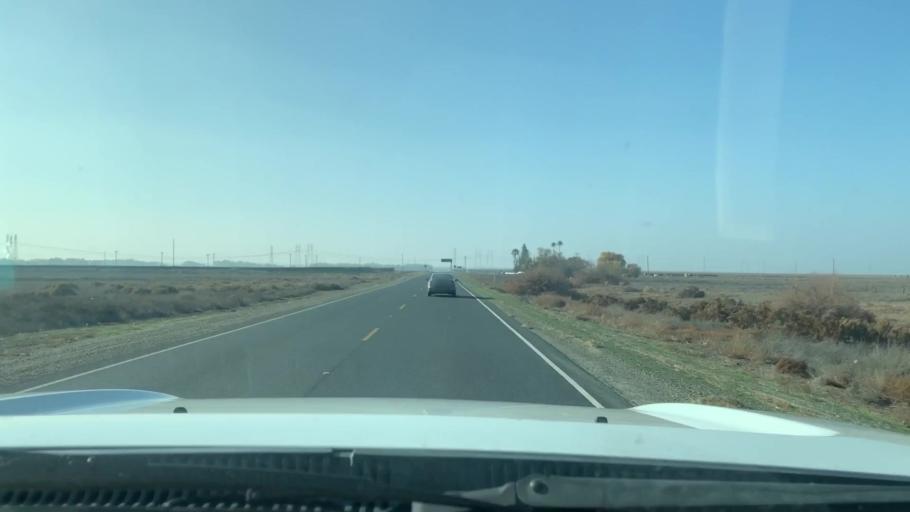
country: US
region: California
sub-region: Kern County
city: Lost Hills
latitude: 35.6160
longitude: -119.6117
